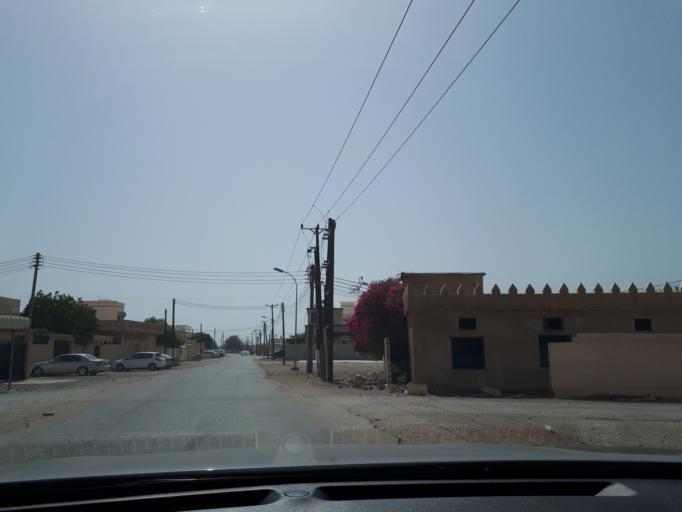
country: OM
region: Al Batinah
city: Barka'
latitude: 23.7064
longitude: 57.9265
